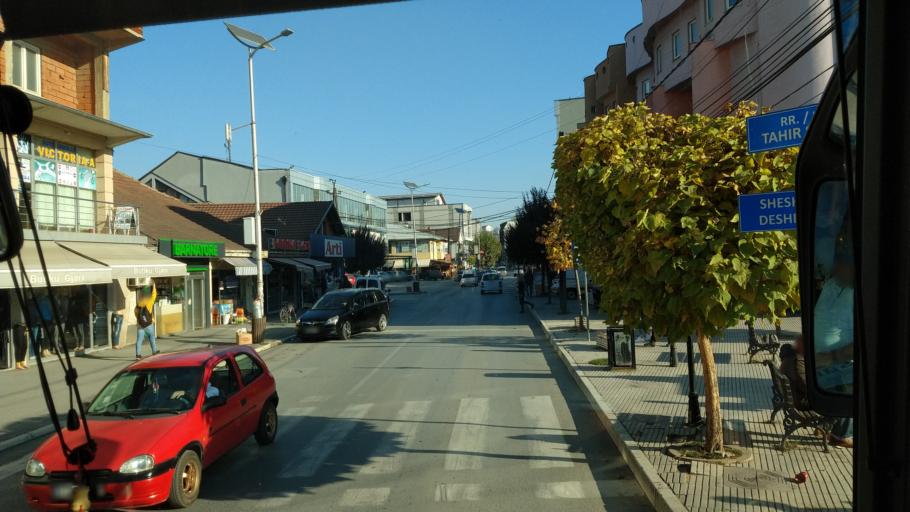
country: XK
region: Ferizaj
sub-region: Komuna e Shtimes
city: Shtime
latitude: 42.4339
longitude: 21.0371
